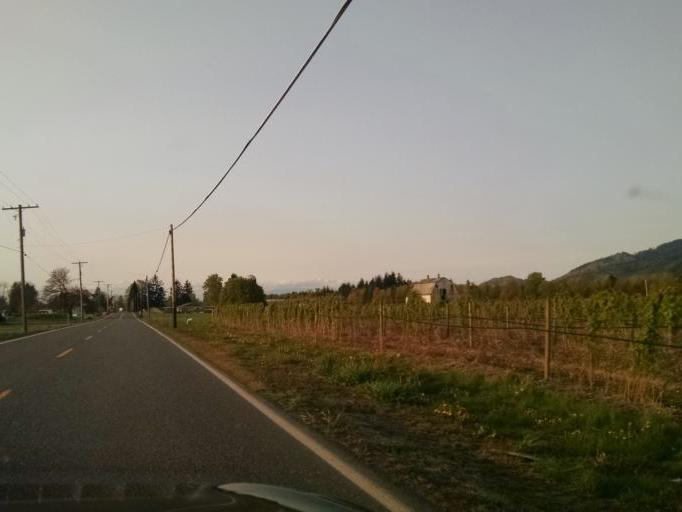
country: US
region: Washington
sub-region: Whatcom County
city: Nooksack
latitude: 48.8740
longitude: -122.3096
